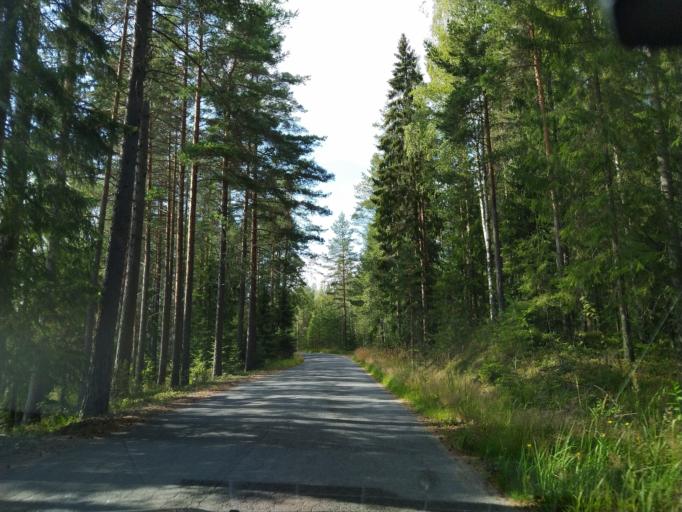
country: FI
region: Uusimaa
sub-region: Helsinki
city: Karkkila
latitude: 60.7177
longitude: 24.1949
